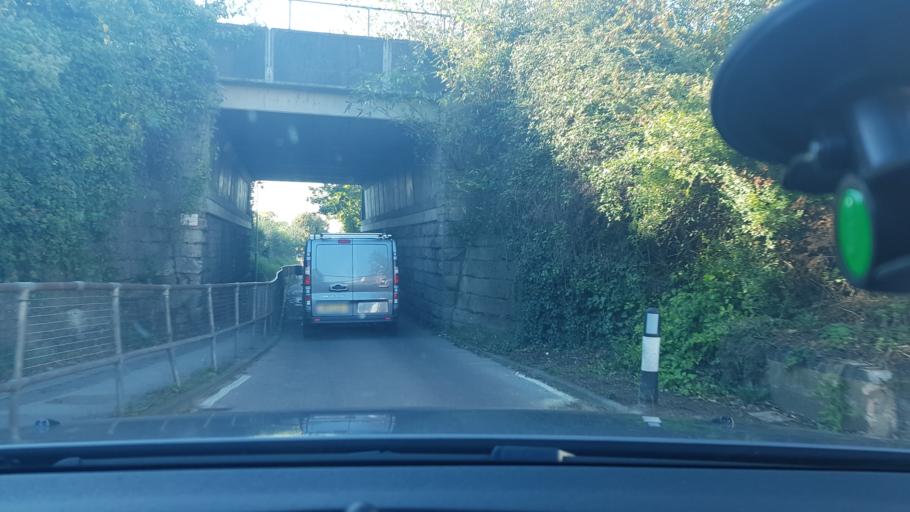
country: GB
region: England
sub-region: Gloucestershire
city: Gloucester
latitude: 51.8343
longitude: -2.2503
